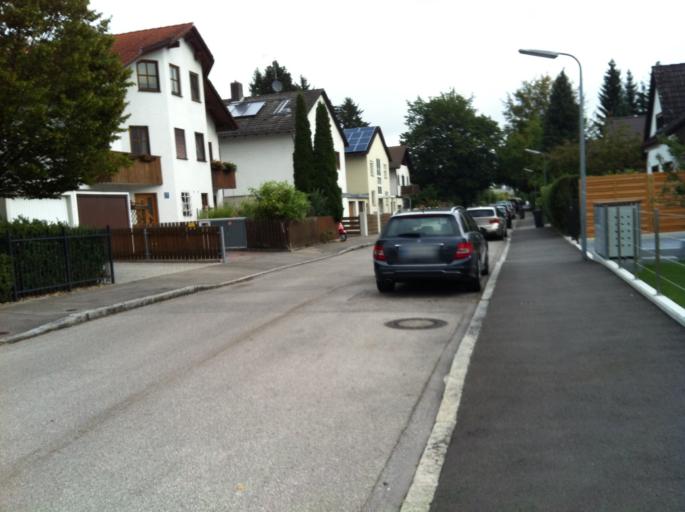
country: DE
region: Bavaria
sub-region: Upper Bavaria
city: Unterfoehring
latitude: 48.1969
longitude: 11.6243
